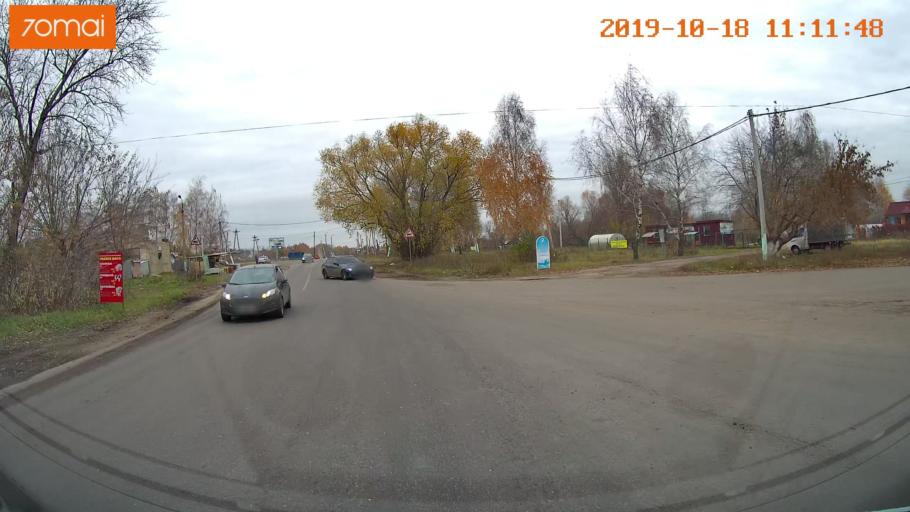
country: RU
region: Tula
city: Kimovsk
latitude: 53.9617
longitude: 38.5518
